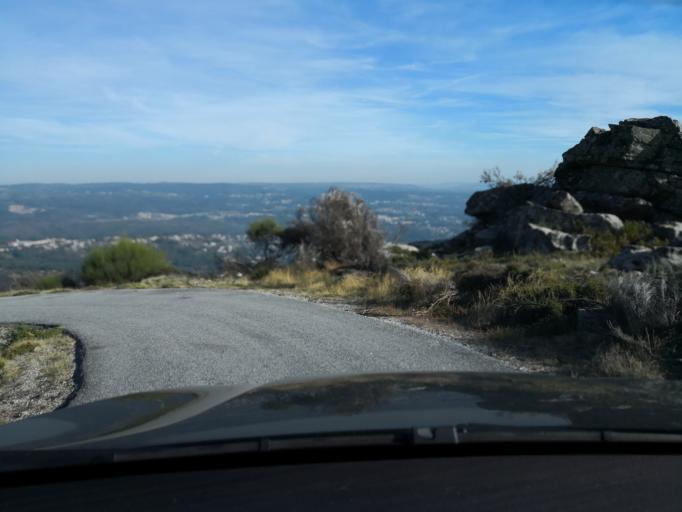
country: PT
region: Vila Real
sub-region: Vila Real
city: Vila Real
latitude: 41.3428
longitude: -7.7636
